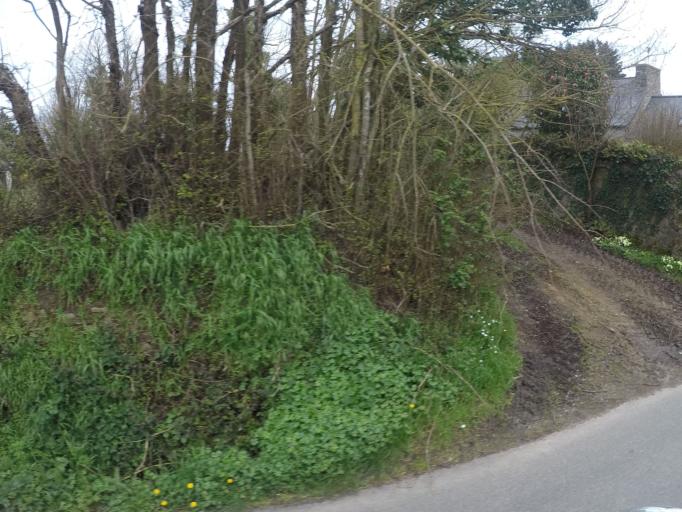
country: FR
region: Brittany
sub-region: Departement des Cotes-d'Armor
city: Plouha
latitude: 48.7057
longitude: -2.9363
